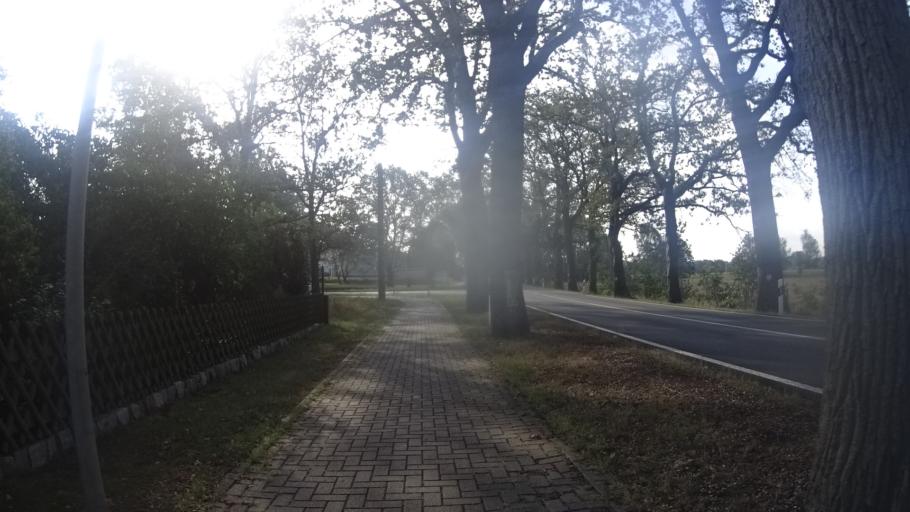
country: DE
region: Brandenburg
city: Wittenberge
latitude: 53.0074
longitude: 11.7152
